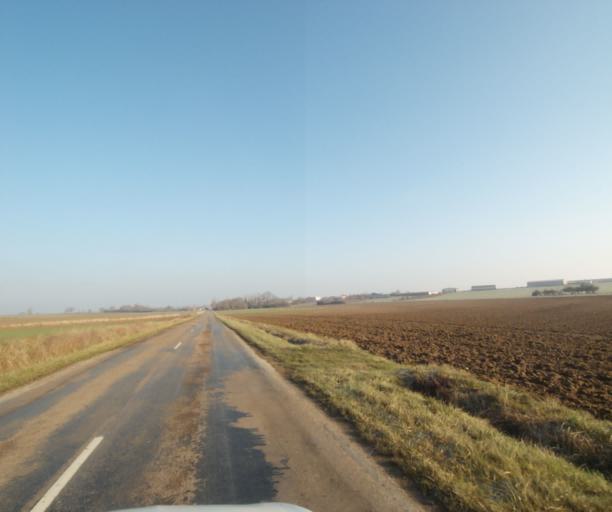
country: FR
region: Champagne-Ardenne
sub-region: Departement de la Haute-Marne
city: Montier-en-Der
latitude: 48.4456
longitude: 4.7609
